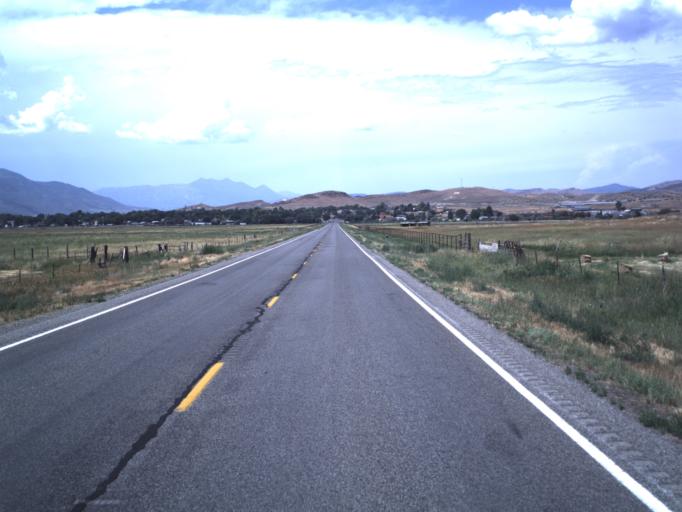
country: US
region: Utah
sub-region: Sanpete County
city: Moroni
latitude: 39.5100
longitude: -111.5699
